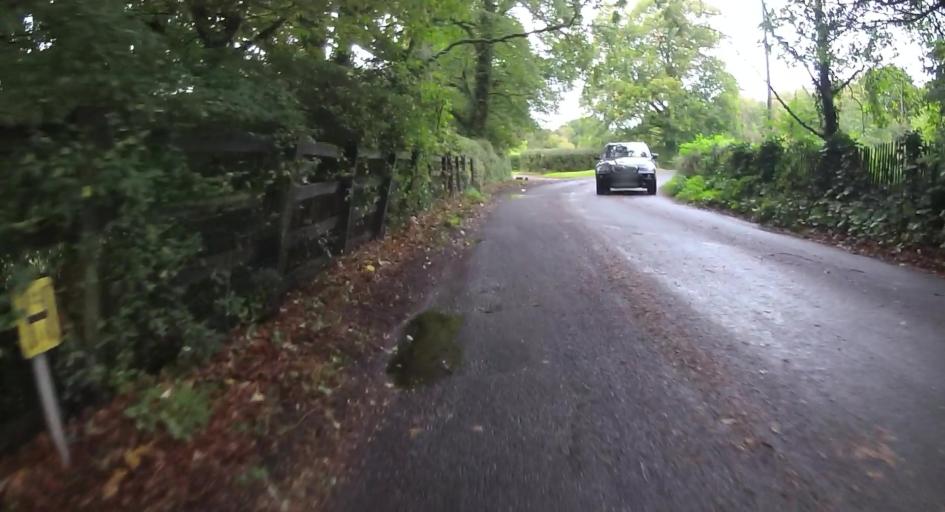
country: GB
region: England
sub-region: Hampshire
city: Tadley
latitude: 51.4067
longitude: -1.1724
